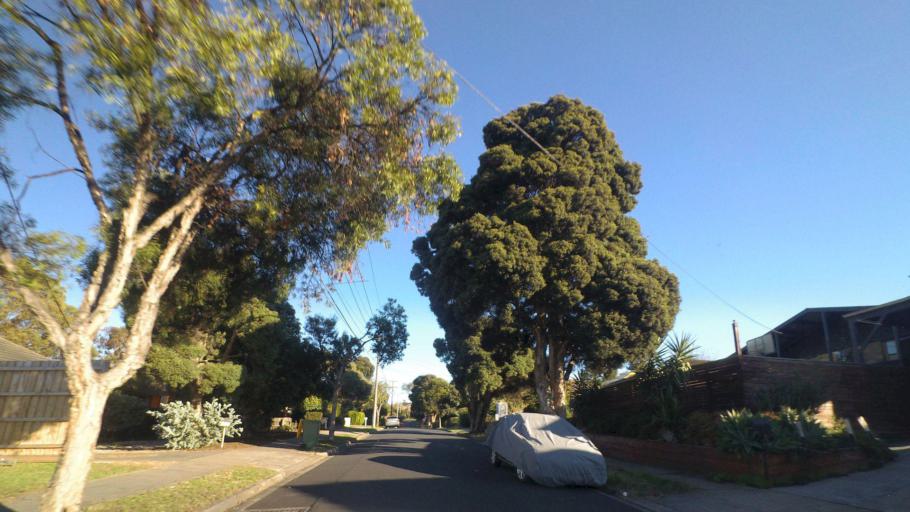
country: AU
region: Victoria
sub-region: Banyule
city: Yallambie
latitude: -37.7313
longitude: 145.0964
